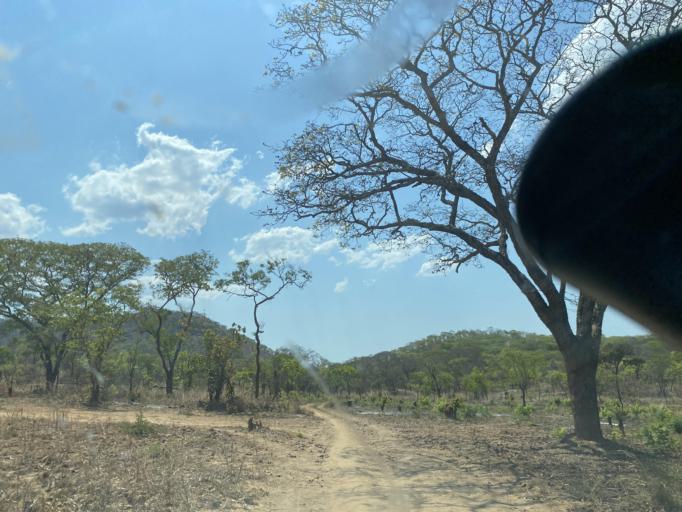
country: ZM
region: Lusaka
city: Chongwe
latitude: -15.0826
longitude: 29.4710
